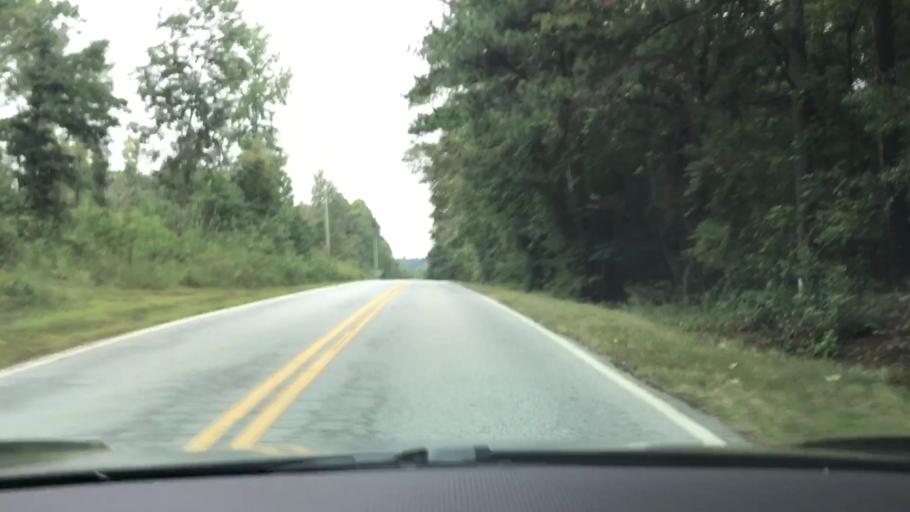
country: US
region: Georgia
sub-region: Barrow County
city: Auburn
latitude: 34.0524
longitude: -83.8200
